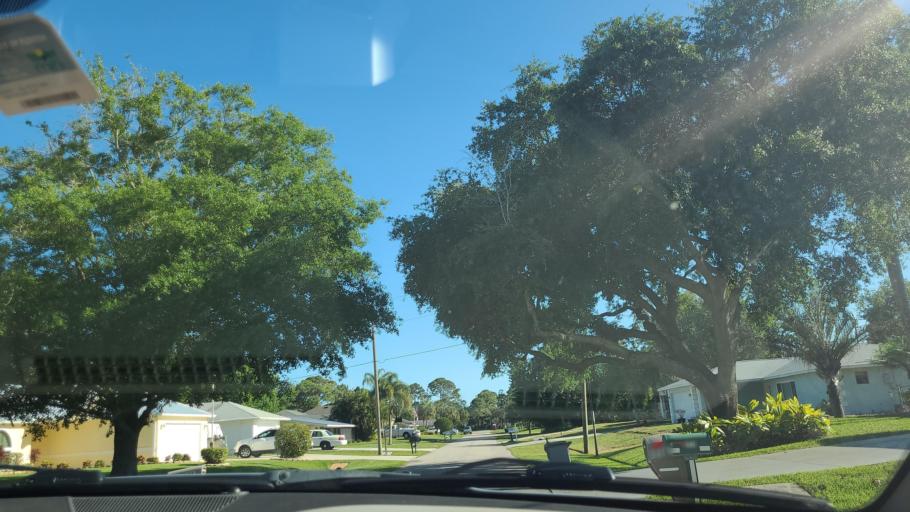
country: US
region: Florida
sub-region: Indian River County
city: Sebastian
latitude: 27.8027
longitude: -80.4912
